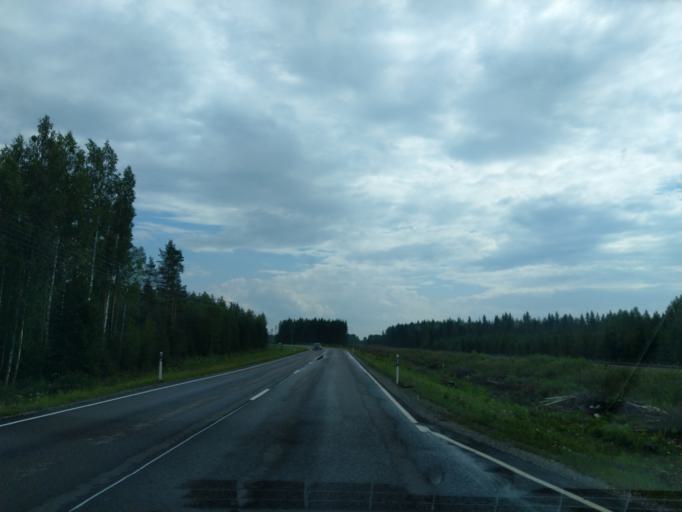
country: FI
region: South Karelia
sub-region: Imatra
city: Parikkala
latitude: 61.6289
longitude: 29.4326
